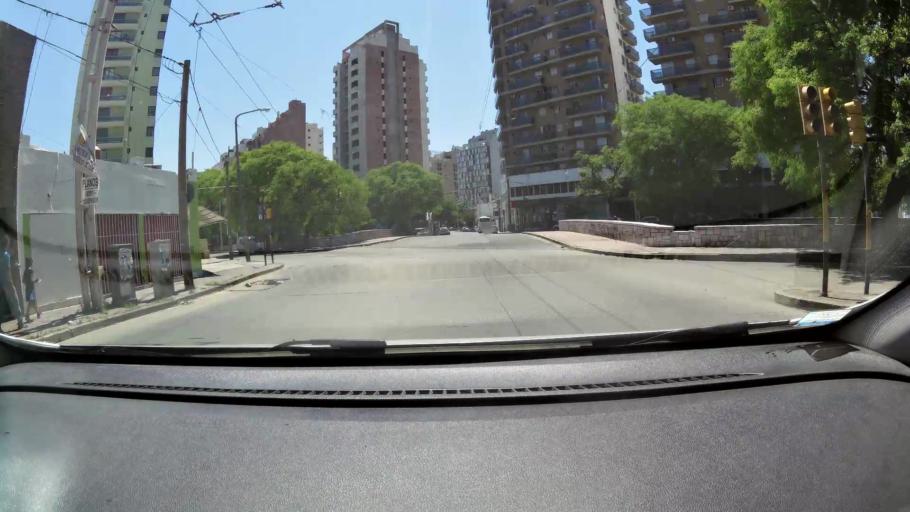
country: AR
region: Cordoba
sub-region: Departamento de Capital
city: Cordoba
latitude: -31.4271
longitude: -64.1950
